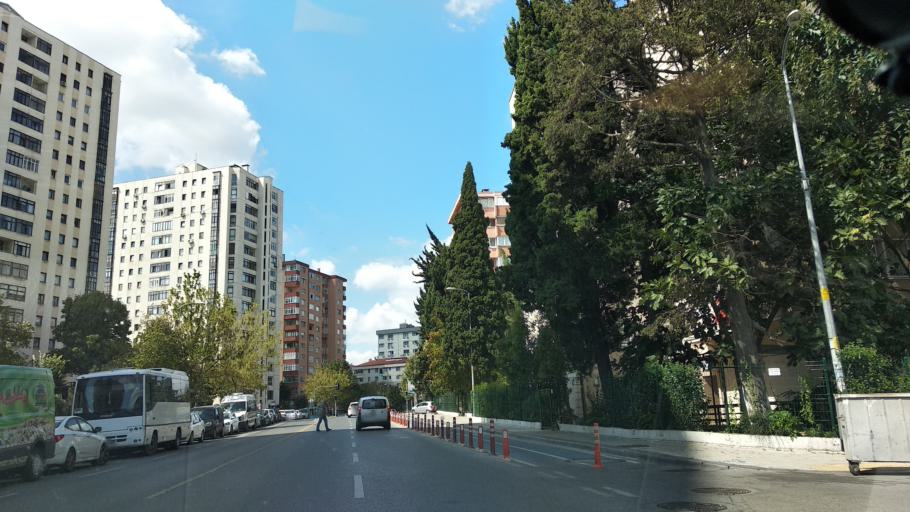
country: TR
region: Istanbul
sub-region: Atasehir
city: Atasehir
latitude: 40.9779
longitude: 29.0951
